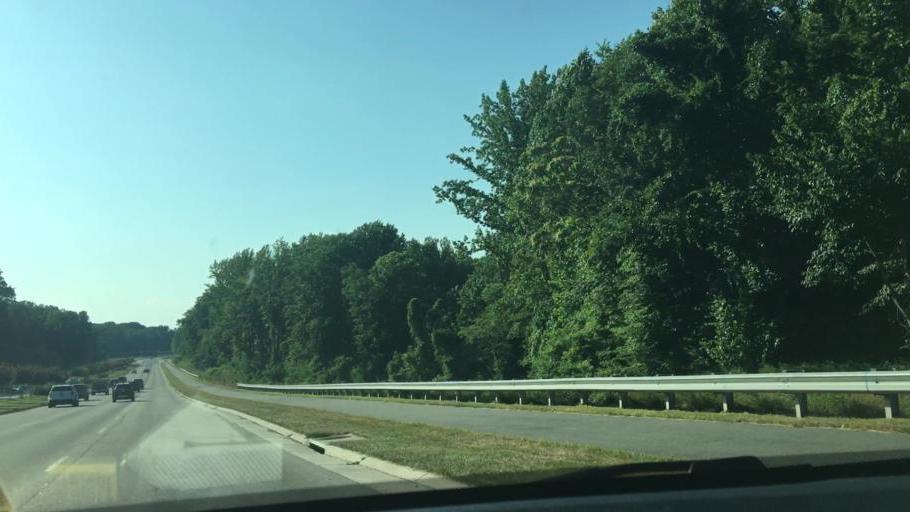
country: US
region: Virginia
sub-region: Prince William County
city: Dale City
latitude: 38.6551
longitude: -77.3180
